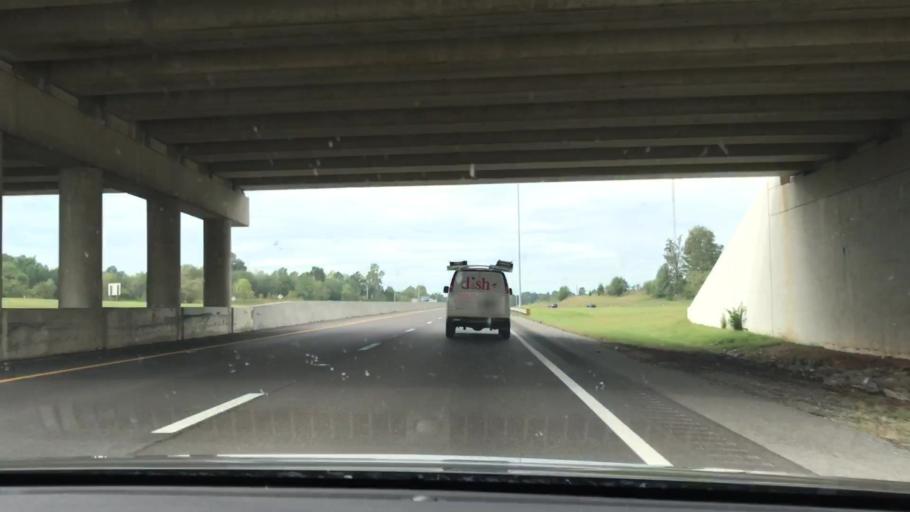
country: US
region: Kentucky
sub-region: Graves County
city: Mayfield
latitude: 36.7570
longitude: -88.6567
